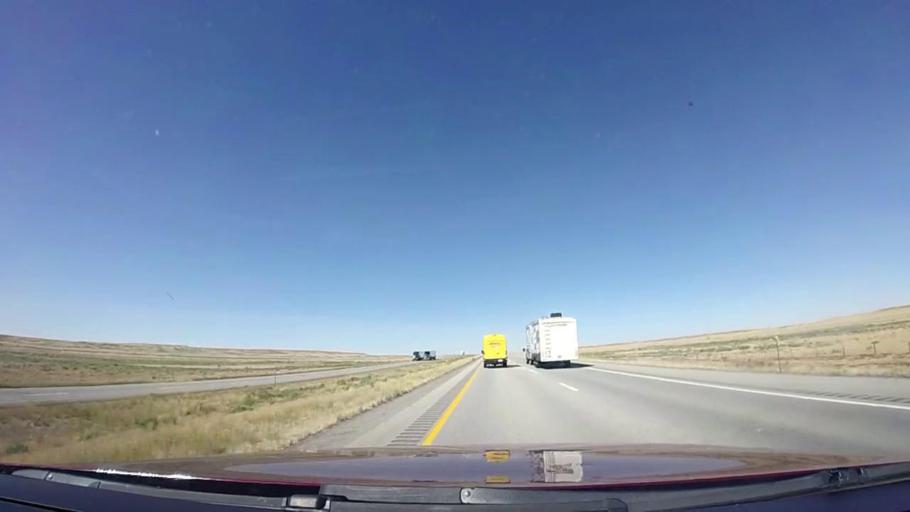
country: US
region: Wyoming
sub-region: Carbon County
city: Rawlins
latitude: 41.6618
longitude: -108.0594
